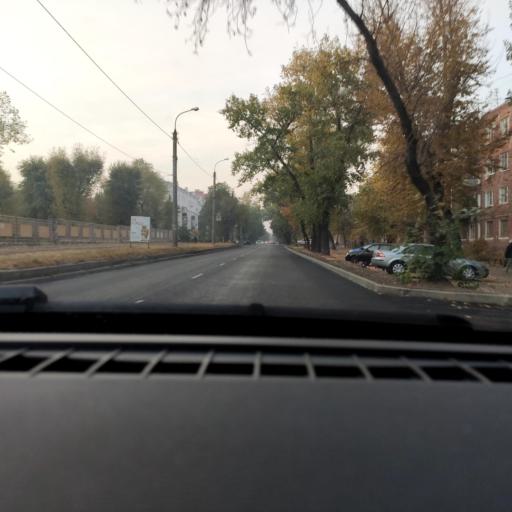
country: RU
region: Voronezj
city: Voronezh
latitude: 51.6414
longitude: 39.2406
